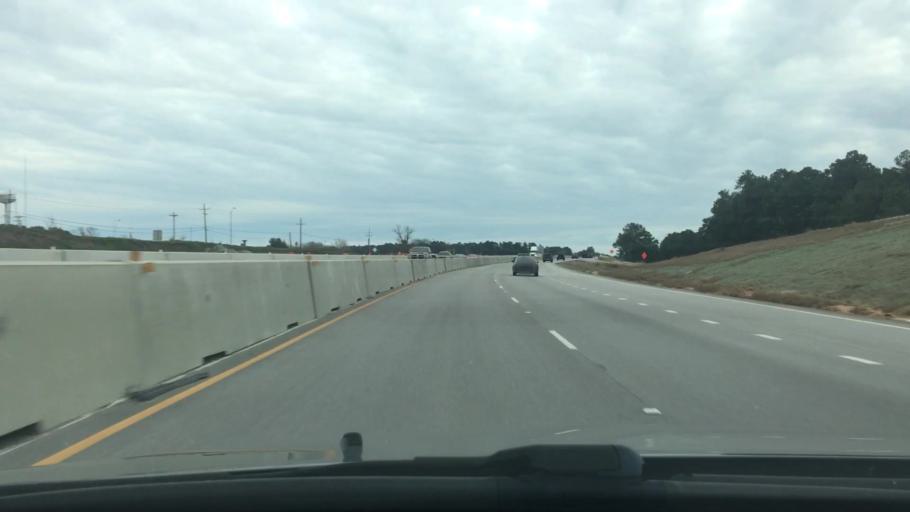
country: US
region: Texas
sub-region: Walker County
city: Huntsville
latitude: 30.6755
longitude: -95.5197
